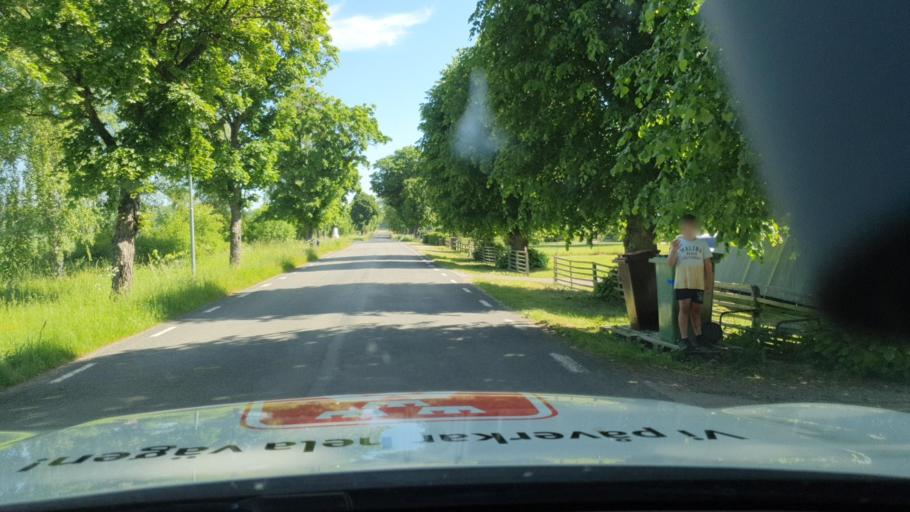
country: SE
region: Vaestra Goetaland
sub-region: Tidaholms Kommun
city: Olofstorp
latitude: 58.2730
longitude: 13.9145
